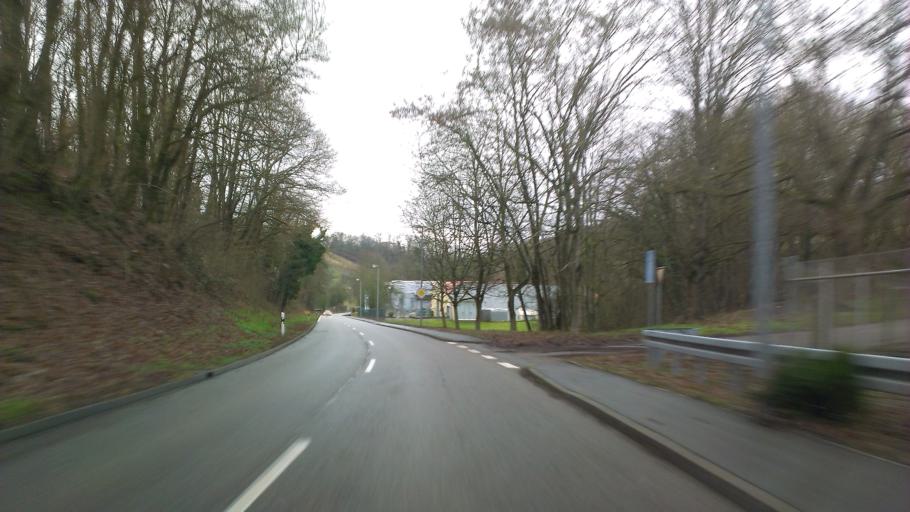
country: DE
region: Baden-Wuerttemberg
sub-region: Karlsruhe Region
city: Sternenfels
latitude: 49.0548
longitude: 8.8514
